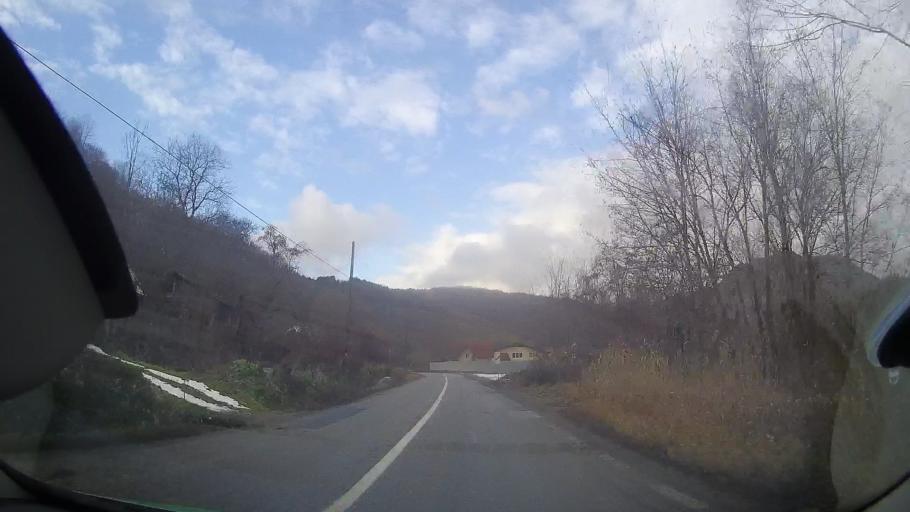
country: RO
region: Alba
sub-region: Comuna Ocolis
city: Ocolis
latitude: 46.4337
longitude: 23.4582
